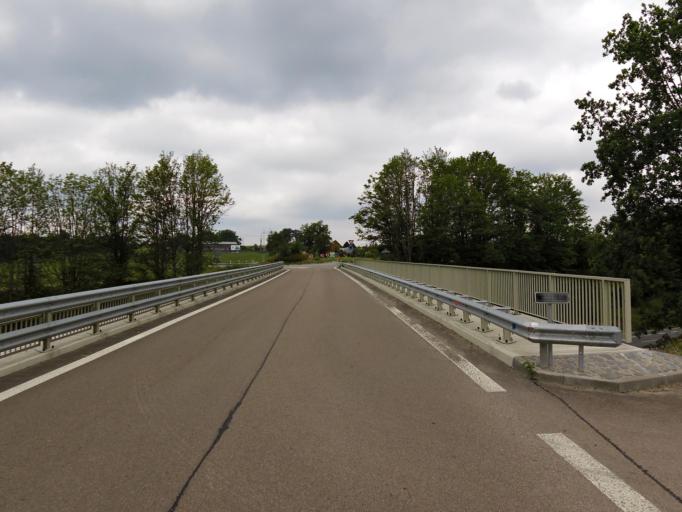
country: CZ
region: Central Bohemia
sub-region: Okres Benesov
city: Cercany
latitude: 49.8710
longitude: 14.7081
